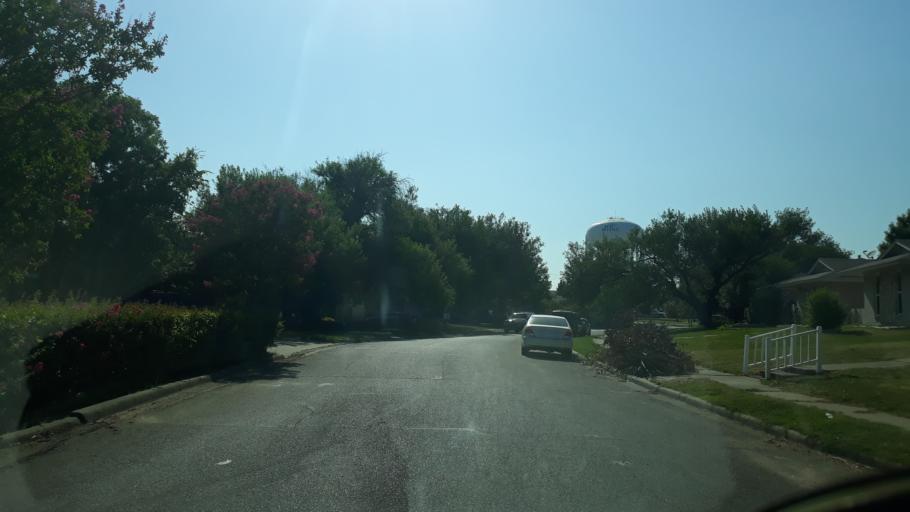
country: US
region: Texas
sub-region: Dallas County
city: Irving
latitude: 32.8440
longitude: -97.0069
